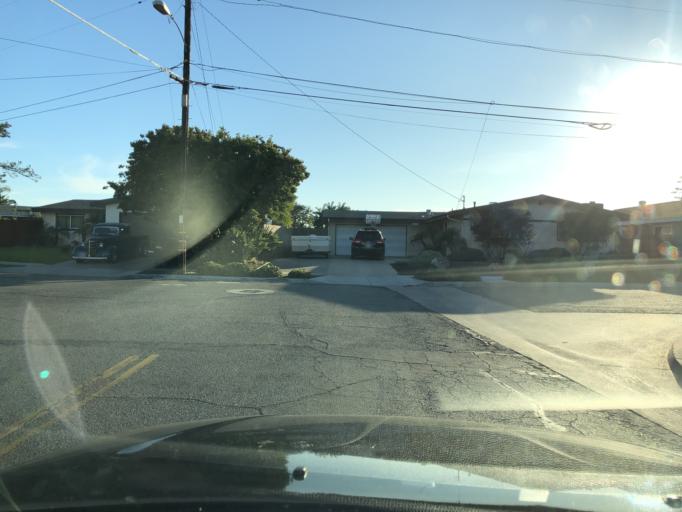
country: US
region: California
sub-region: San Diego County
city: La Jolla
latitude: 32.8158
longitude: -117.1962
